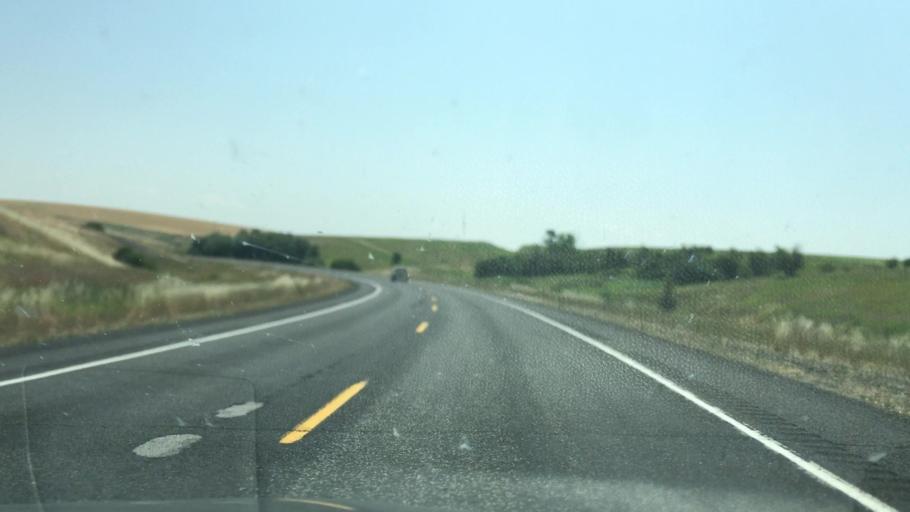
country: US
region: Idaho
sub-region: Lewis County
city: Nezperce
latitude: 46.2211
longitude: -116.4361
